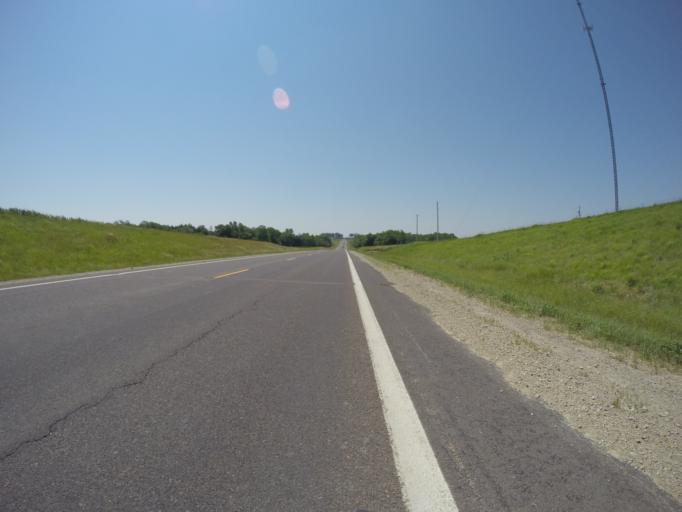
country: US
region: Kansas
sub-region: Doniphan County
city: Highland
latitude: 39.8467
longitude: -95.2652
